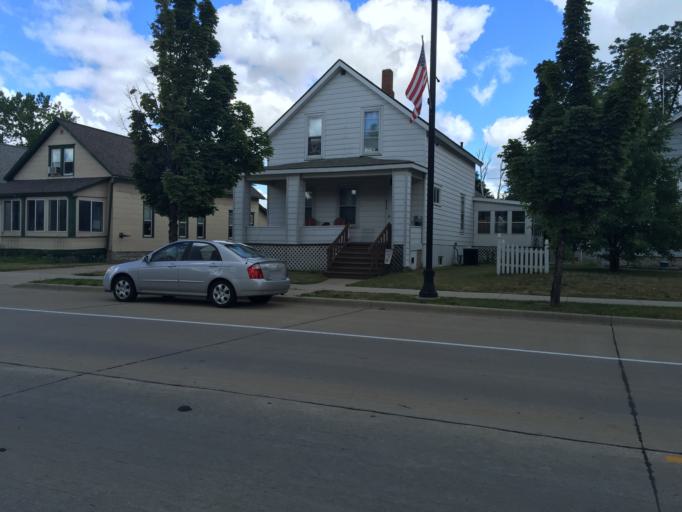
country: US
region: Wisconsin
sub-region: Marinette County
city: Marinette
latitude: 45.0994
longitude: -87.6419
